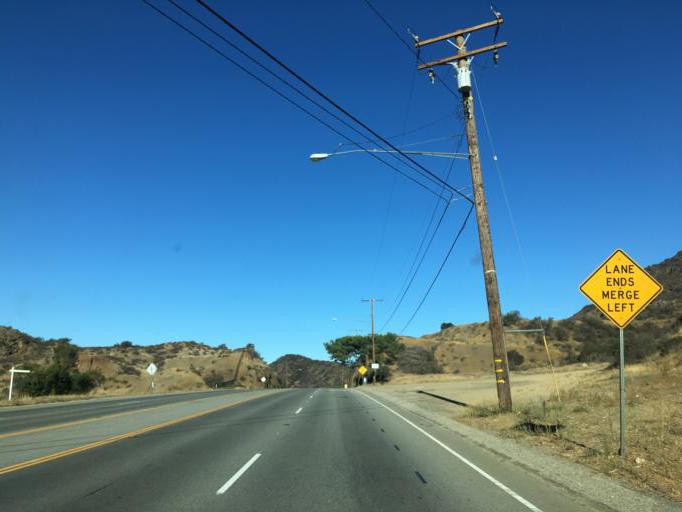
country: US
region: California
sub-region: Los Angeles County
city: Agoura Hills
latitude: 34.1300
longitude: -118.7700
